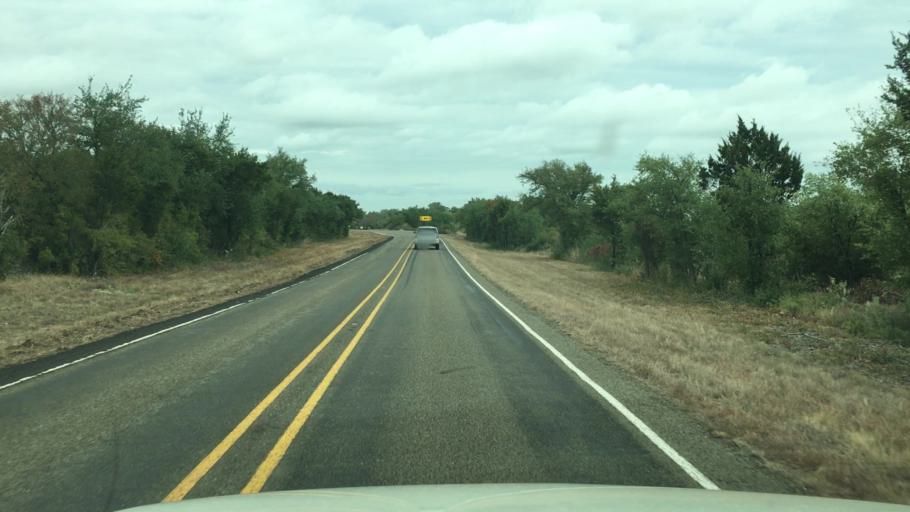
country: US
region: Texas
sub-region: Llano County
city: Horseshoe Bay
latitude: 30.4759
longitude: -98.4167
